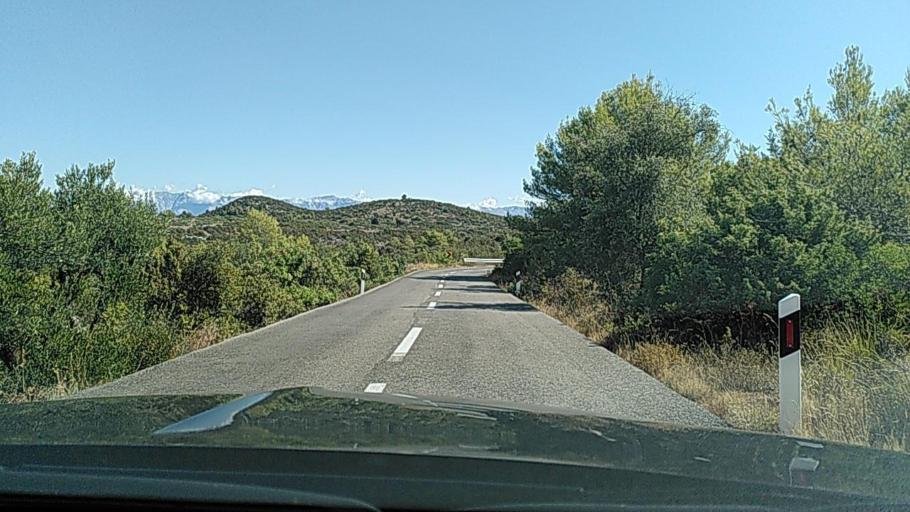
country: HR
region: Splitsko-Dalmatinska
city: Jelsa
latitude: 43.1436
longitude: 16.8228
